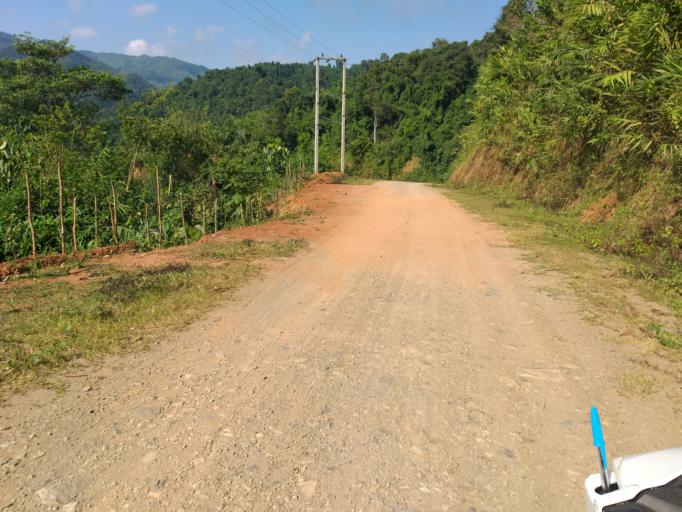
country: LA
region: Phongsali
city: Khoa
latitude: 21.1977
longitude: 102.6664
